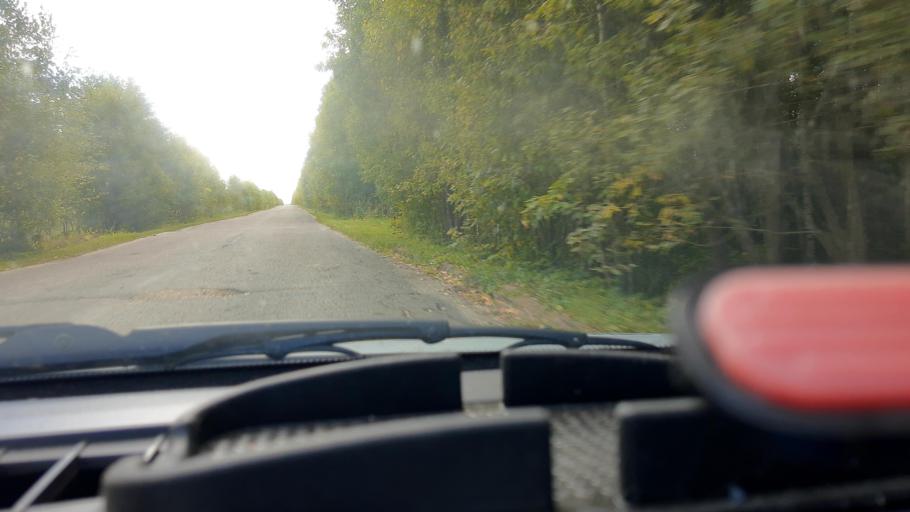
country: RU
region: Mariy-El
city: Kilemary
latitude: 56.9047
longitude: 46.7374
